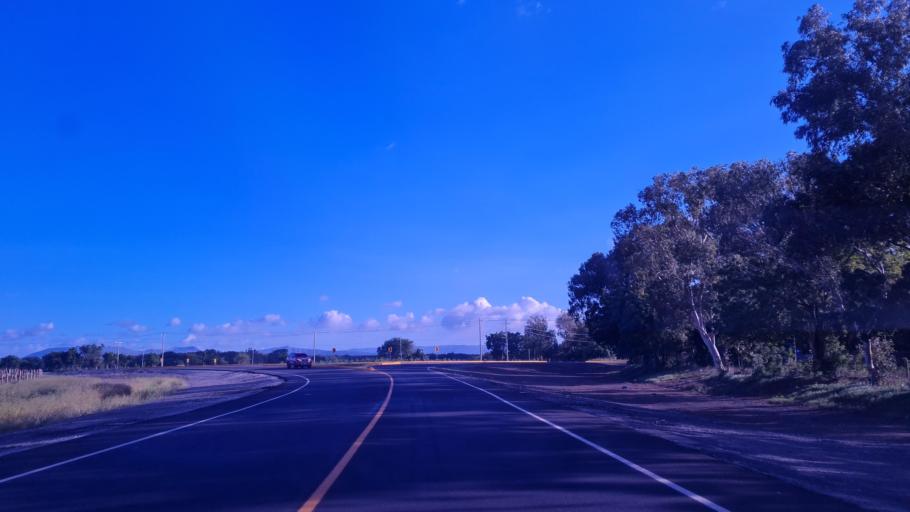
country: NI
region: Masaya
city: Ticuantepe
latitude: 12.1063
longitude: -86.1555
